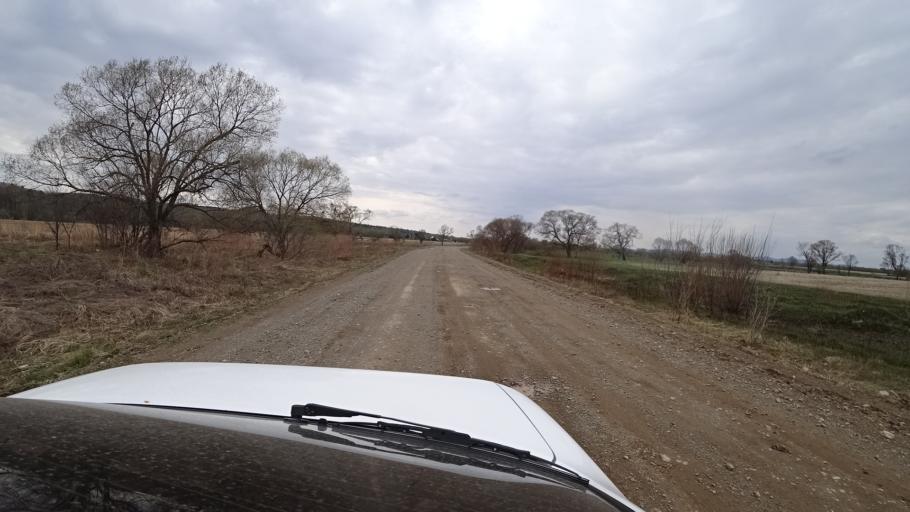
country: RU
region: Primorskiy
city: Novopokrovka
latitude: 45.4898
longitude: 134.4592
